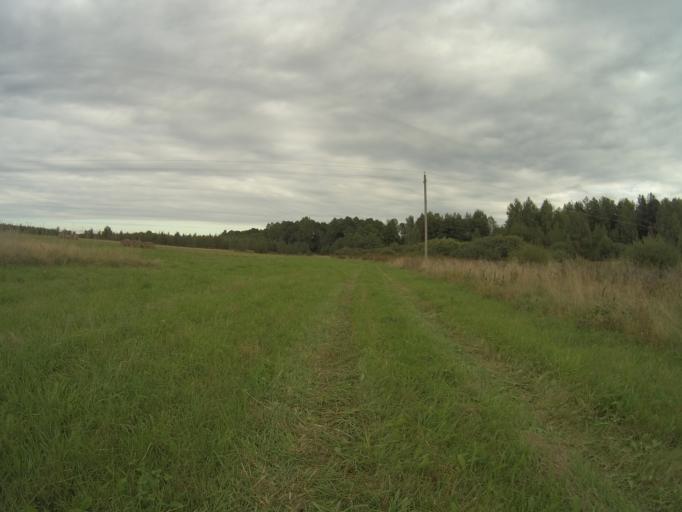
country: RU
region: Vladimir
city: Golovino
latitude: 55.9568
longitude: 40.4941
